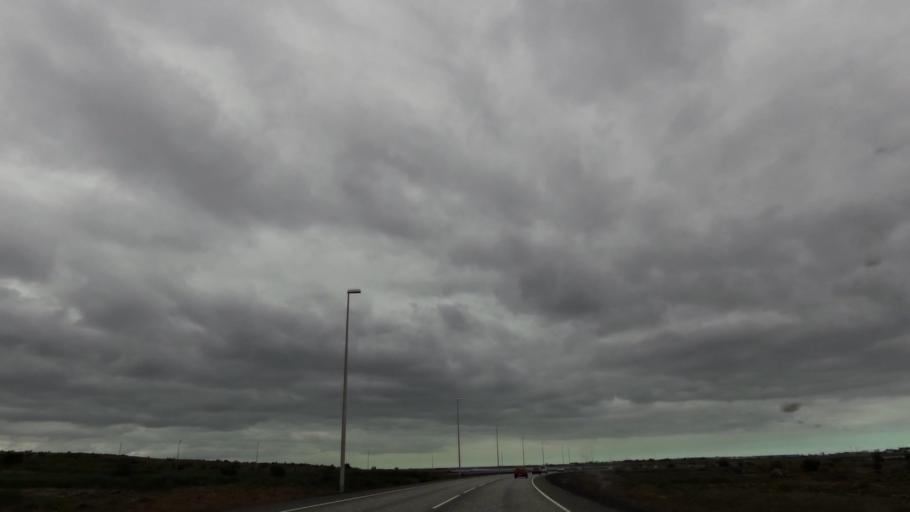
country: IS
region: Capital Region
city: Alftanes
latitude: 64.0907
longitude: -21.9802
